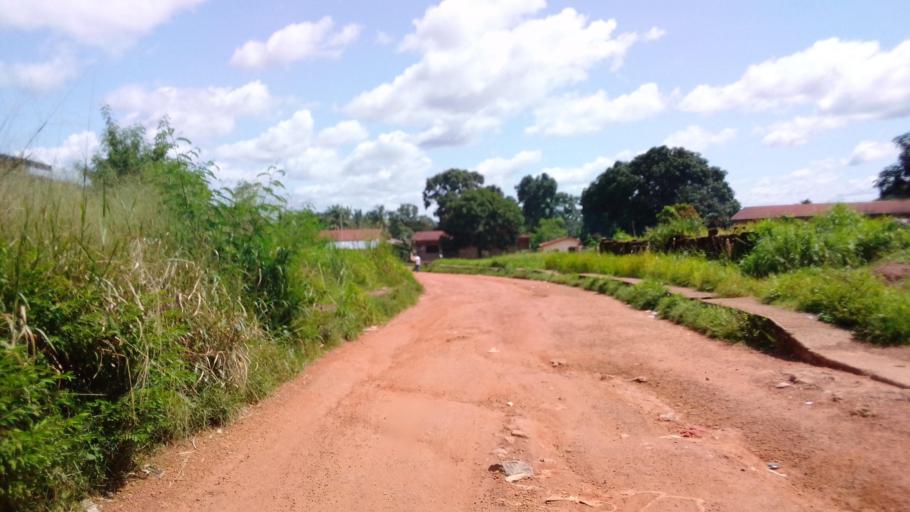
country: SL
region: Northern Province
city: Makeni
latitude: 8.8829
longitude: -12.0409
